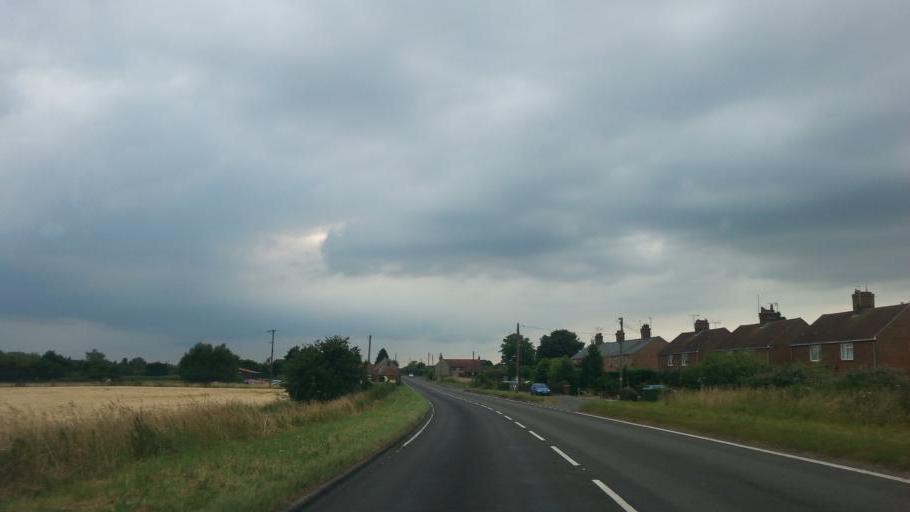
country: GB
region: England
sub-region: Norfolk
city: Fakenham
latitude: 52.8264
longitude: 0.7208
